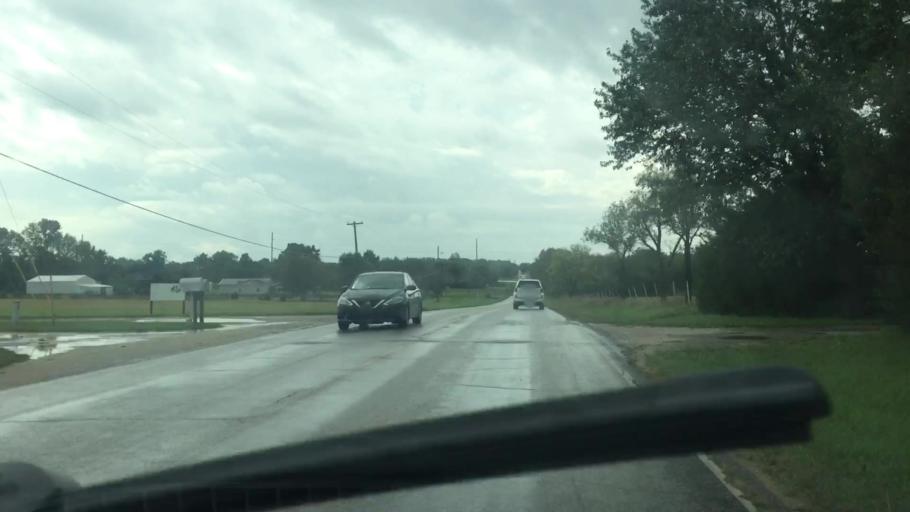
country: US
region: Kansas
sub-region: Allen County
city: Iola
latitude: 37.8967
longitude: -95.4094
